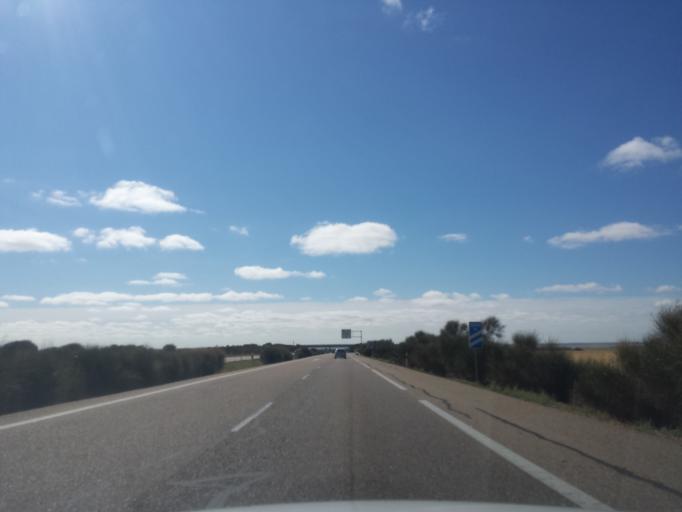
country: ES
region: Castille and Leon
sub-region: Provincia de Zamora
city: Quintanilla del Monte
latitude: 41.8041
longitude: -5.3492
